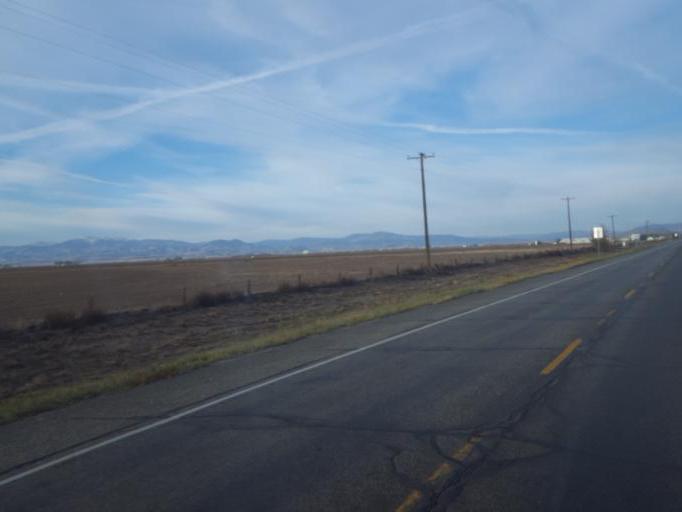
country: US
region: Colorado
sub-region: Saguache County
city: Center
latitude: 37.7482
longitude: -106.1186
